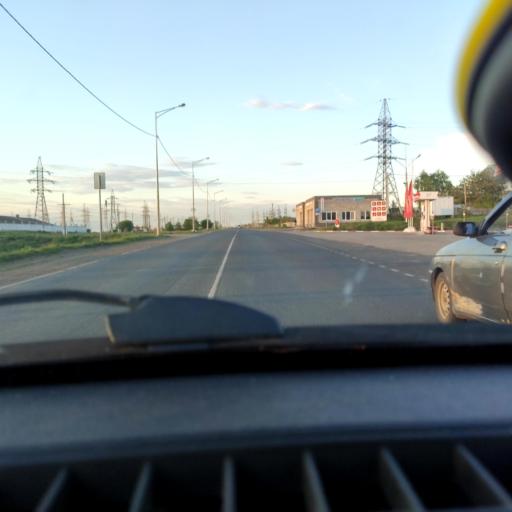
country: RU
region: Samara
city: Zhigulevsk
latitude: 53.5563
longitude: 49.5347
